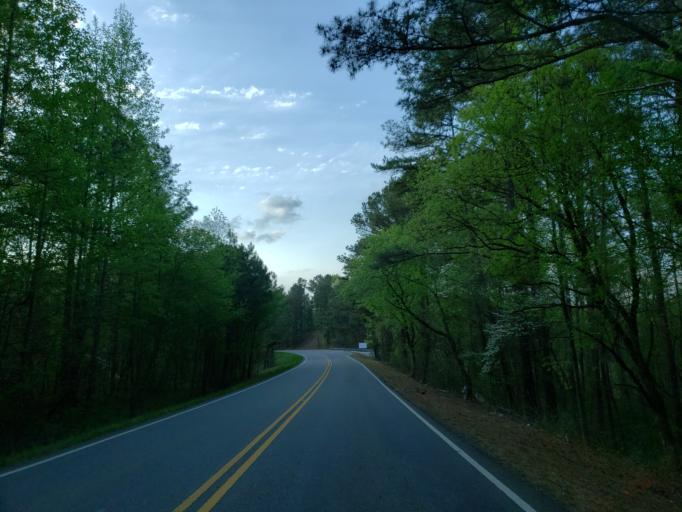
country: US
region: Georgia
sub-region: Cherokee County
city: Ball Ground
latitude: 34.2747
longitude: -84.3720
